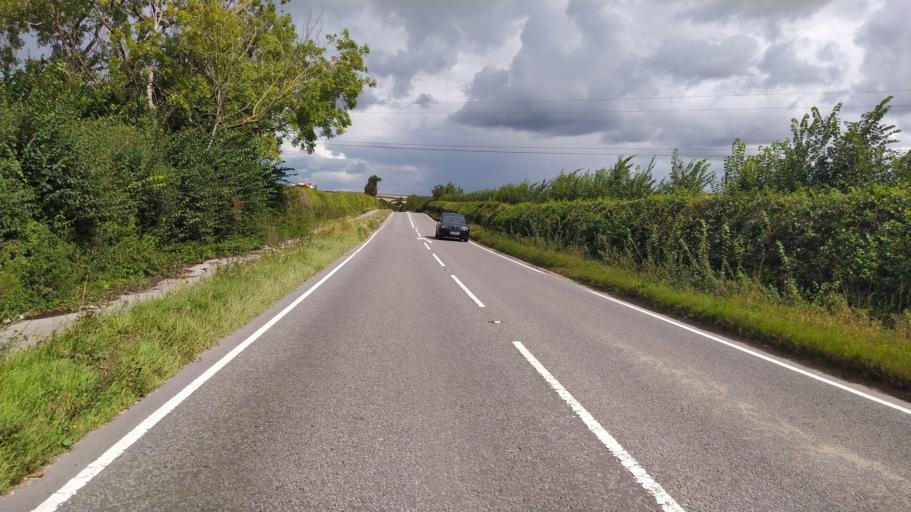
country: GB
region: England
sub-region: Dorset
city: Blandford Forum
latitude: 50.8739
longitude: -2.1427
